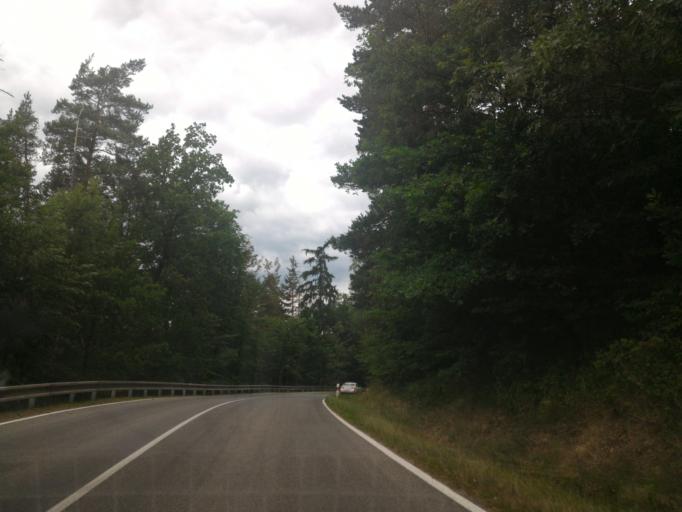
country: CZ
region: Vysocina
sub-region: Okres Pelhrimov
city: Zeliv
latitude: 49.5231
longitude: 15.1710
